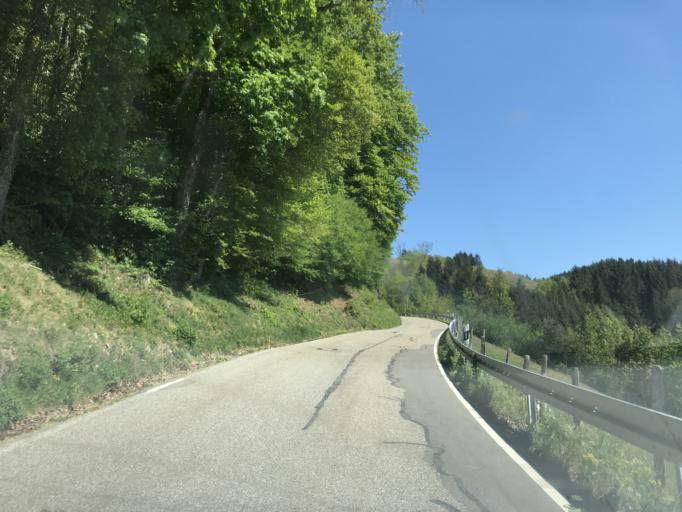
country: DE
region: Baden-Wuerttemberg
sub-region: Freiburg Region
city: Zell im Wiesental
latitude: 47.6800
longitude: 7.8723
